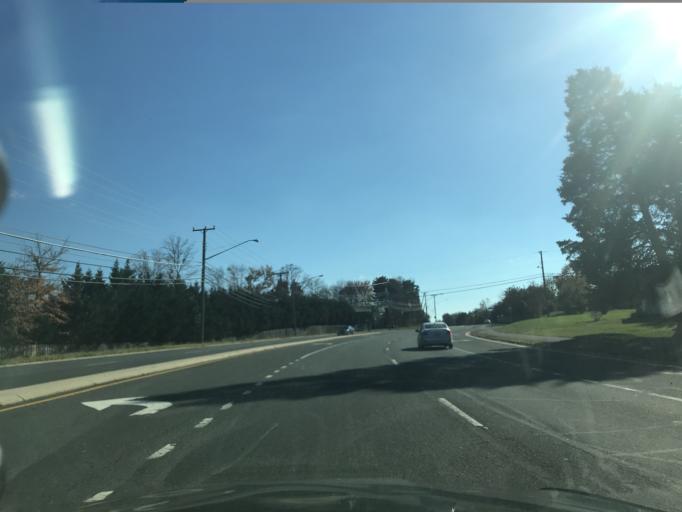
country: US
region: Virginia
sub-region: Fairfax County
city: Oak Hill
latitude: 38.9005
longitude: -77.3815
